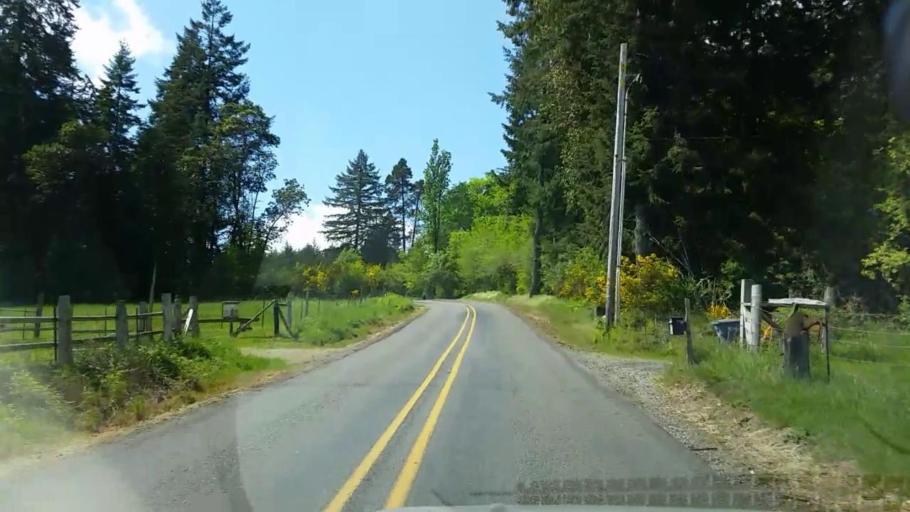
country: US
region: Washington
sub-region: Pierce County
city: Key Center
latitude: 47.3408
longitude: -122.7498
